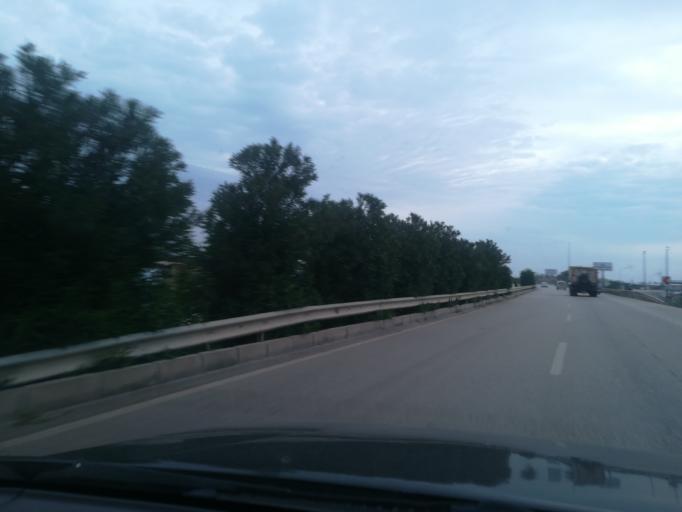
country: TR
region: Adana
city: Yakapinar
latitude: 36.9697
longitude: 35.6432
